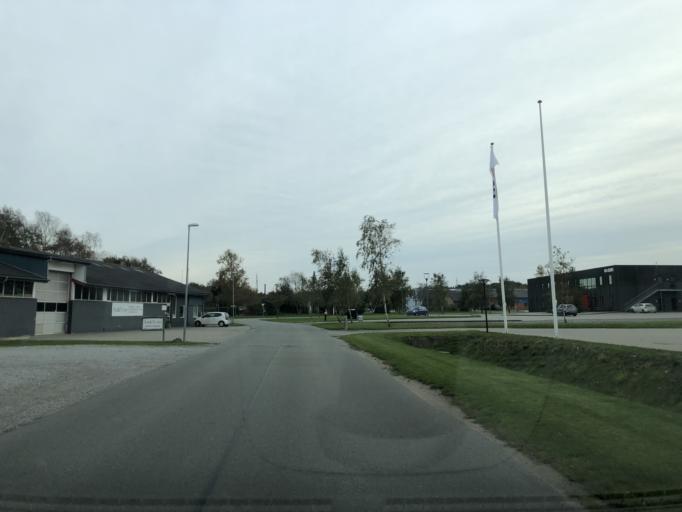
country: DK
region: Central Jutland
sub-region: Syddjurs Kommune
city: Hornslet
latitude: 56.3056
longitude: 10.3132
